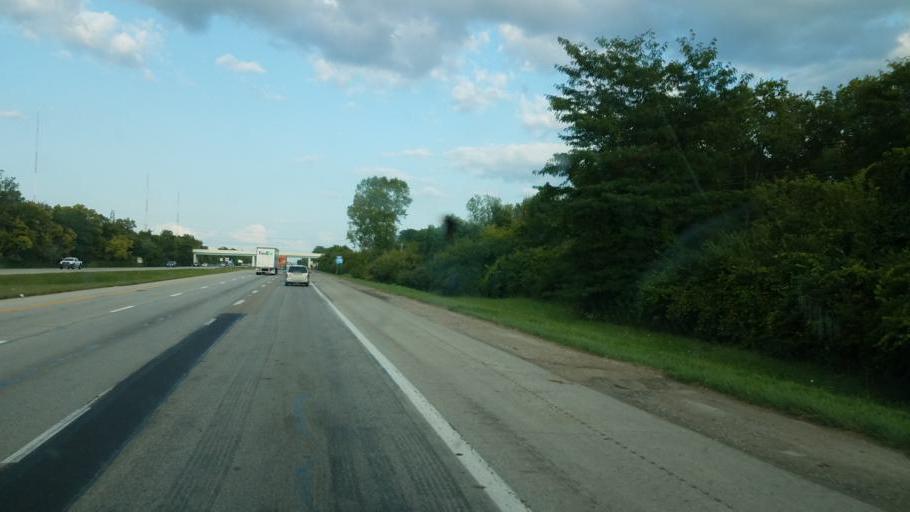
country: US
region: Ohio
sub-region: Franklin County
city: Obetz
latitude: 39.8736
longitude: -82.9927
